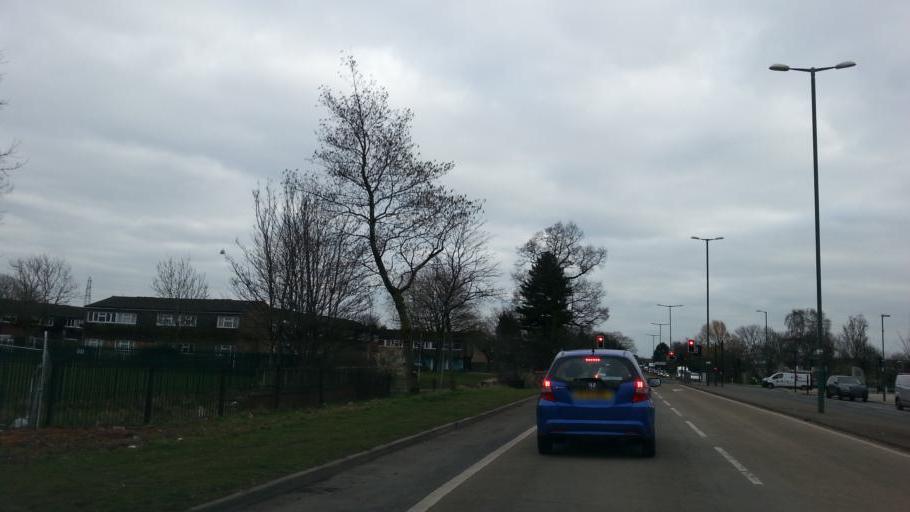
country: GB
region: England
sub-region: Solihull
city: Chelmsley Wood
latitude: 52.4791
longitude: -1.7266
